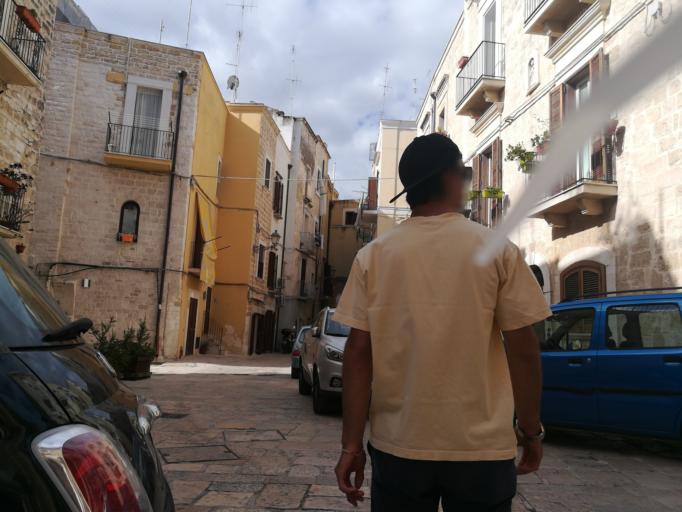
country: IT
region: Apulia
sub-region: Provincia di Bari
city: Bari
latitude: 41.1321
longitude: 16.8708
